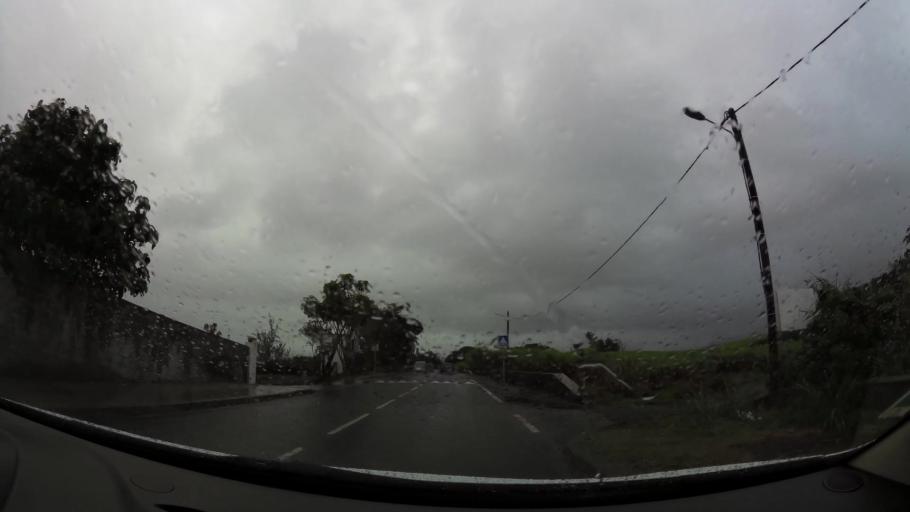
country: RE
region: Reunion
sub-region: Reunion
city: Saint-Benoit
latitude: -21.0208
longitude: 55.7003
